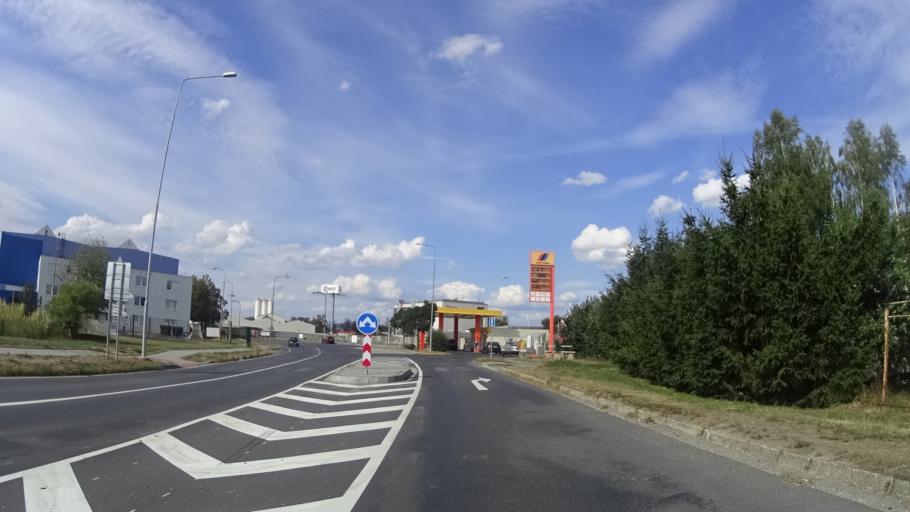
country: CZ
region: Olomoucky
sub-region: Okres Sumperk
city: Mohelnice
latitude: 49.7740
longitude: 16.9411
